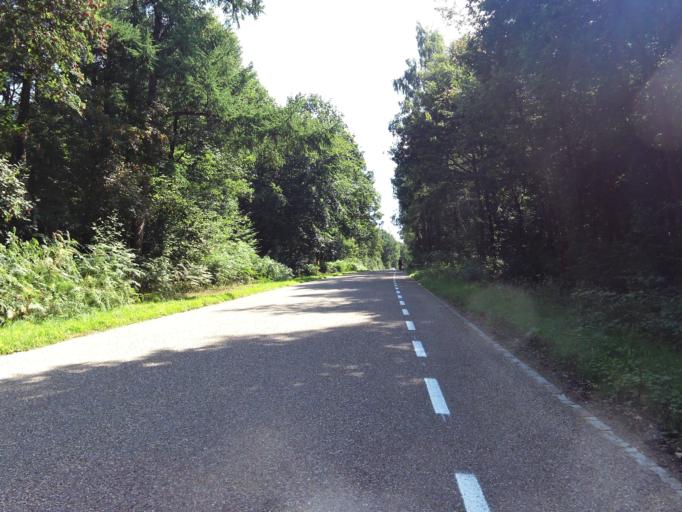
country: BE
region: Wallonia
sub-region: Province de Liege
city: Plombieres
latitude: 50.7674
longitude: 5.9543
